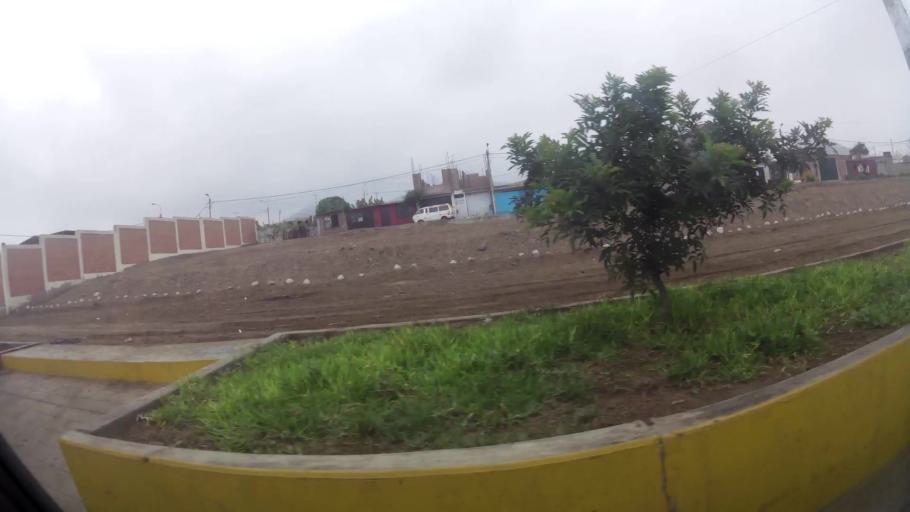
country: PE
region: Lima
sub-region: Provincia de Huaral
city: Chancay
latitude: -11.5885
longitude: -77.2575
